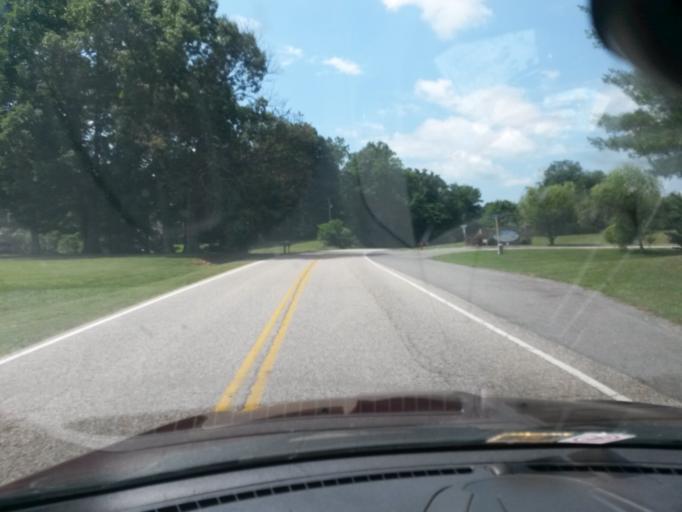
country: US
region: Virginia
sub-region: City of Buena Vista
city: Buena Vista
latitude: 37.9180
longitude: -79.2300
